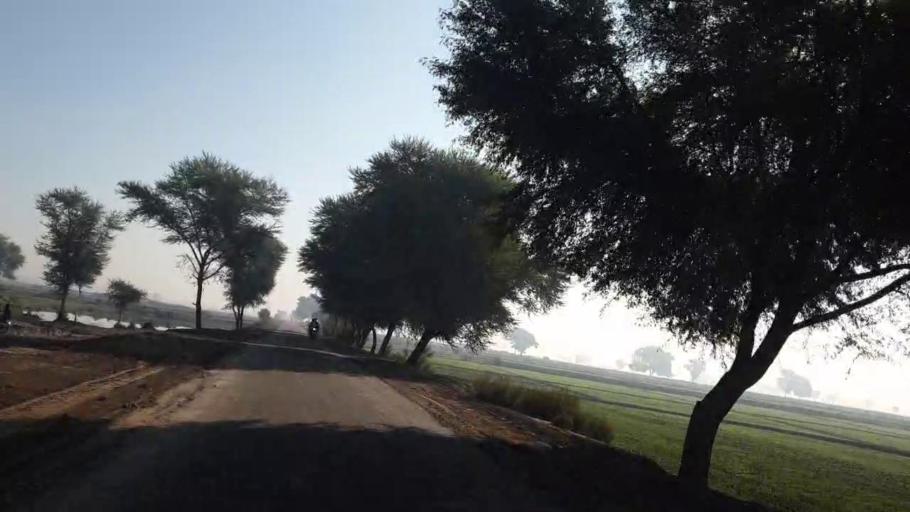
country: PK
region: Sindh
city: Dadu
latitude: 26.6726
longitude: 67.8240
